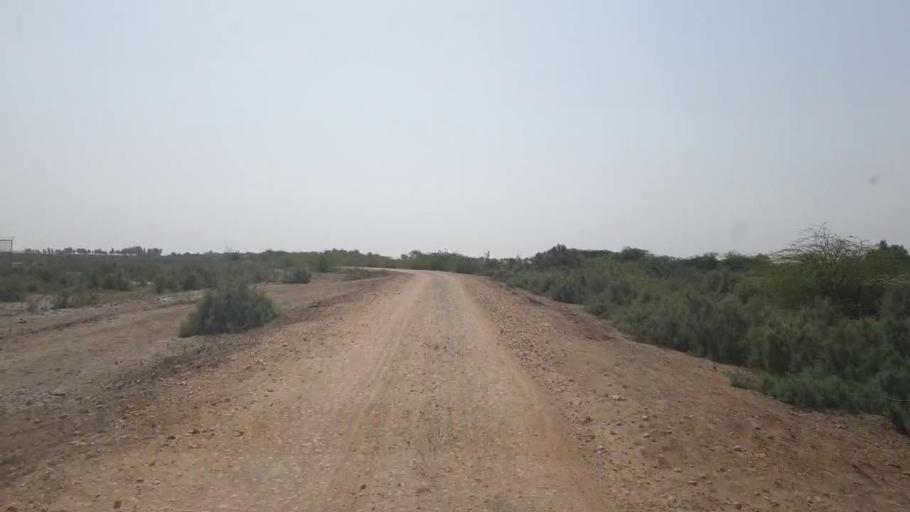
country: PK
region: Sindh
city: Jati
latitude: 24.3862
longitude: 68.5987
